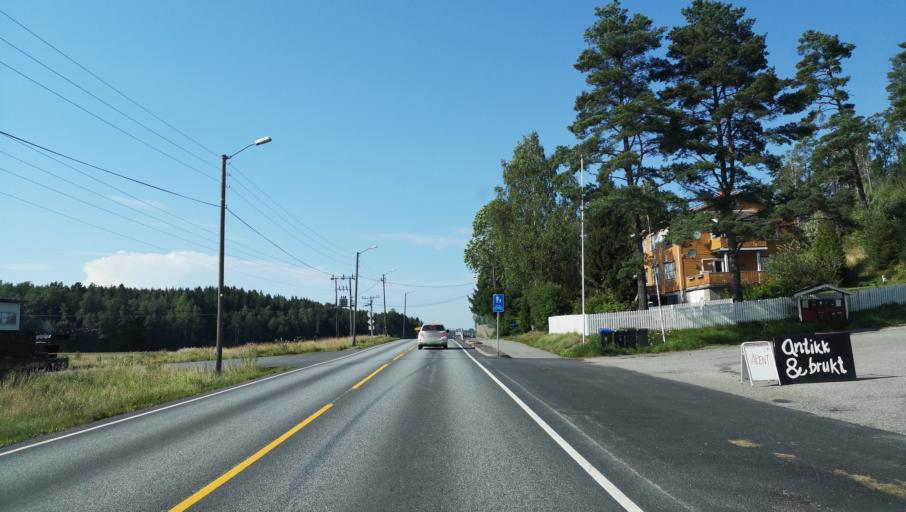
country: NO
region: Ostfold
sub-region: Valer
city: Kirkebygda
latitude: 59.5550
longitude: 10.8416
